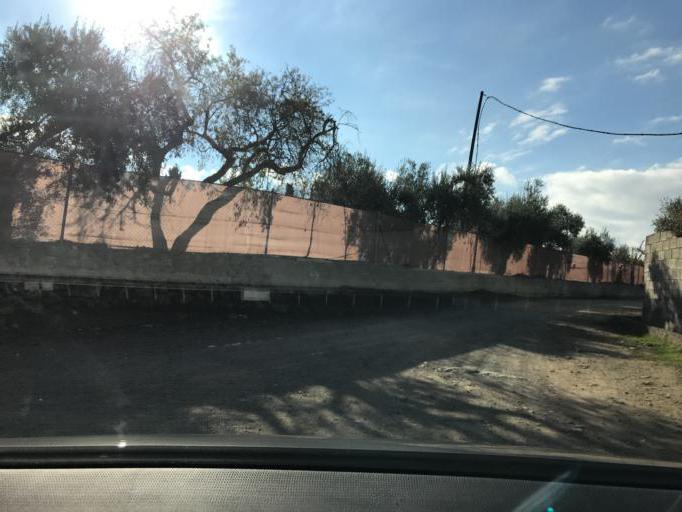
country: ES
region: Andalusia
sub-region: Provincia de Granada
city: Gojar
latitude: 37.0982
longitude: -3.6168
